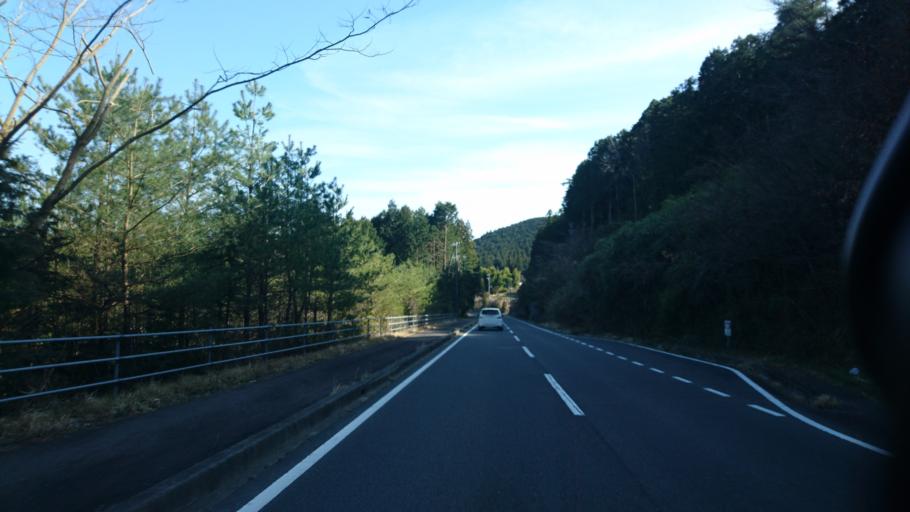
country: JP
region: Gifu
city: Mizunami
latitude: 35.4615
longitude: 137.3542
